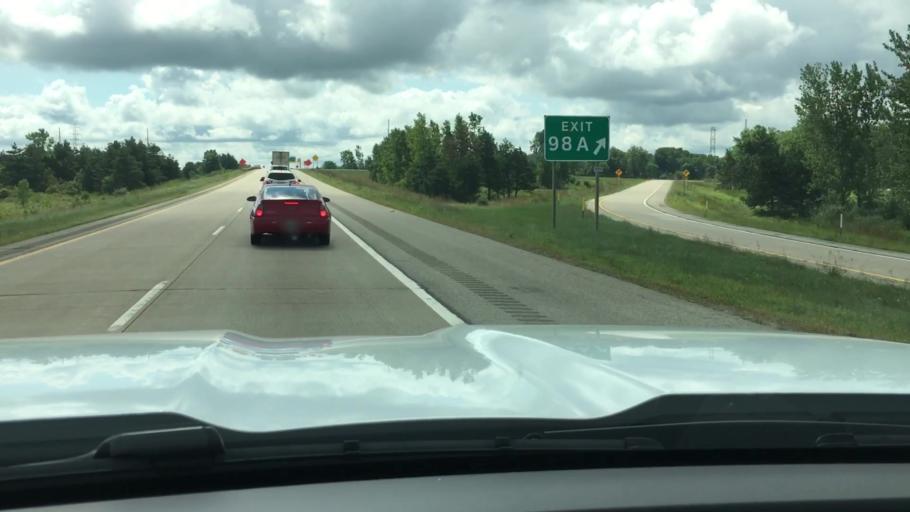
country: US
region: Michigan
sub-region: Eaton County
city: Dimondale
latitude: 42.6796
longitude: -84.6572
